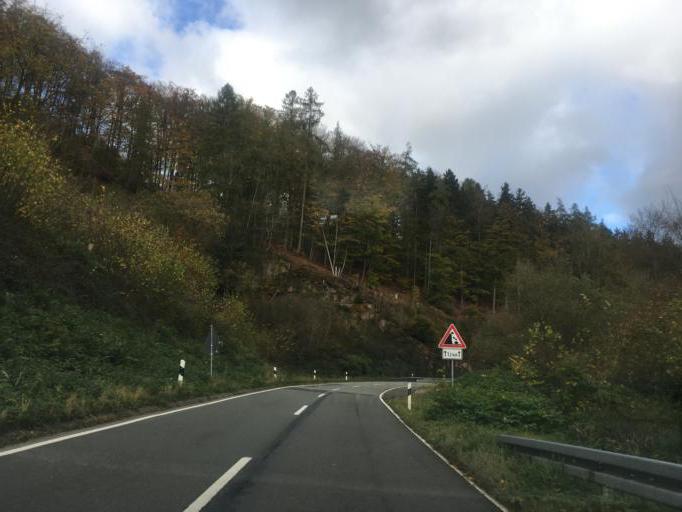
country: DE
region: Lower Saxony
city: Furstenberg
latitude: 51.7374
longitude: 9.4196
